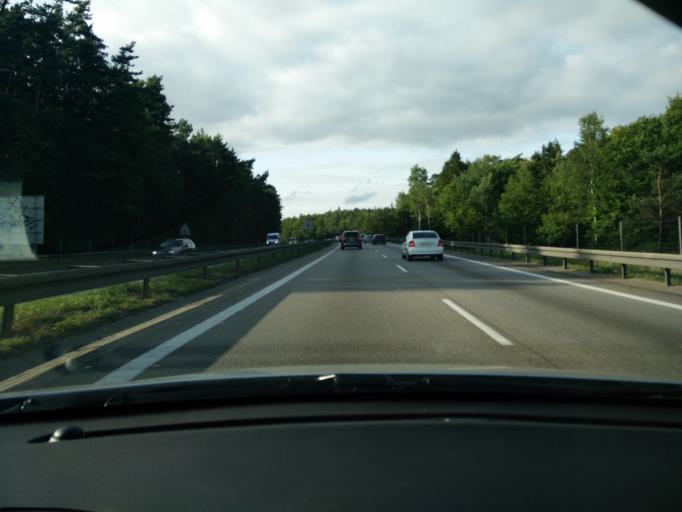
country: PL
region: Pomeranian Voivodeship
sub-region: Gdynia
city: Wielki Kack
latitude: 54.4783
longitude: 18.4727
